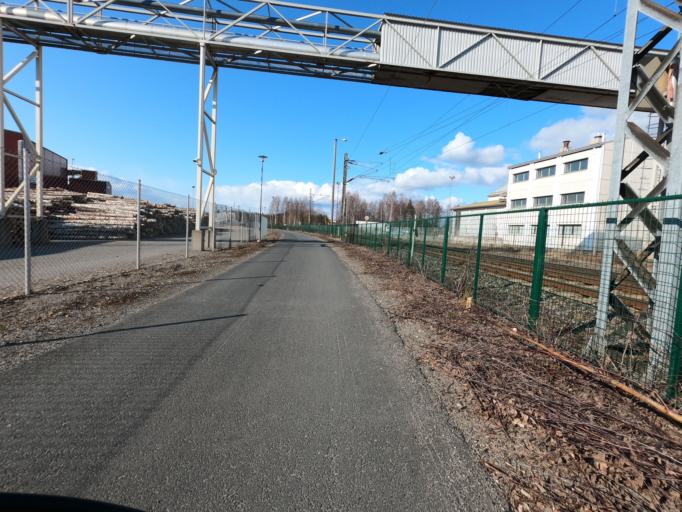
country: FI
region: North Karelia
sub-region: Joensuu
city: Joensuu
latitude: 62.6039
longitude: 29.7804
